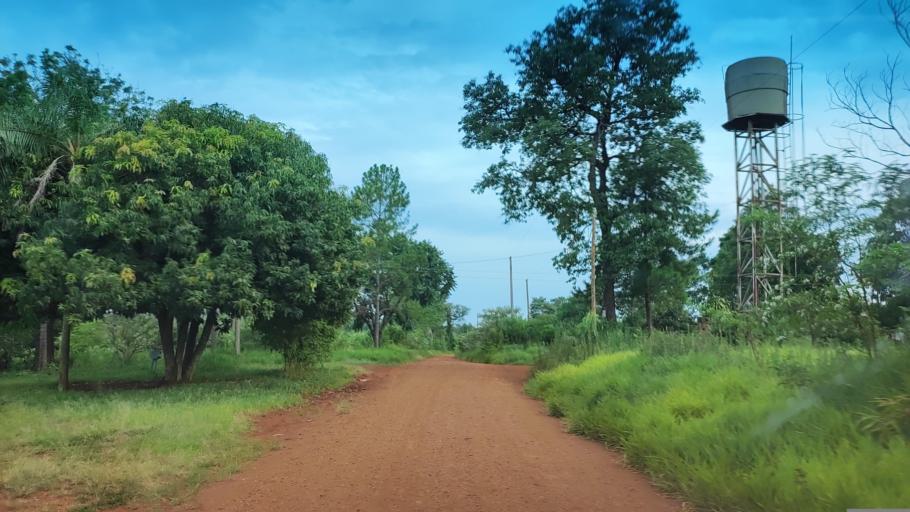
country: AR
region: Misiones
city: Gobernador Roca
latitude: -27.1640
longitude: -55.4570
